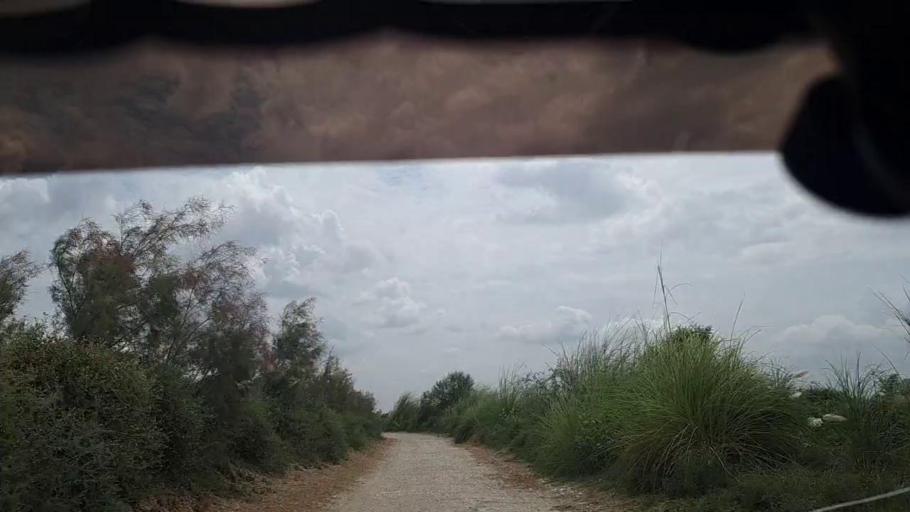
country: PK
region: Sindh
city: Rustam jo Goth
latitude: 28.0506
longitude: 68.9393
